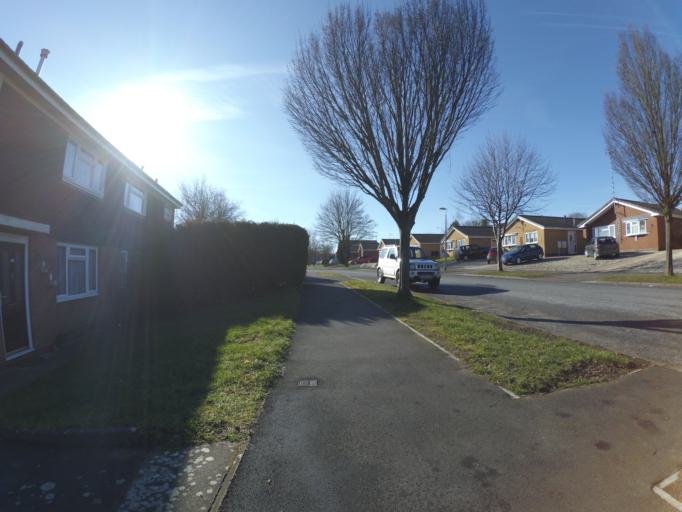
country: GB
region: England
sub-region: Warwickshire
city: Rugby
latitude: 52.3888
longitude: -1.2416
